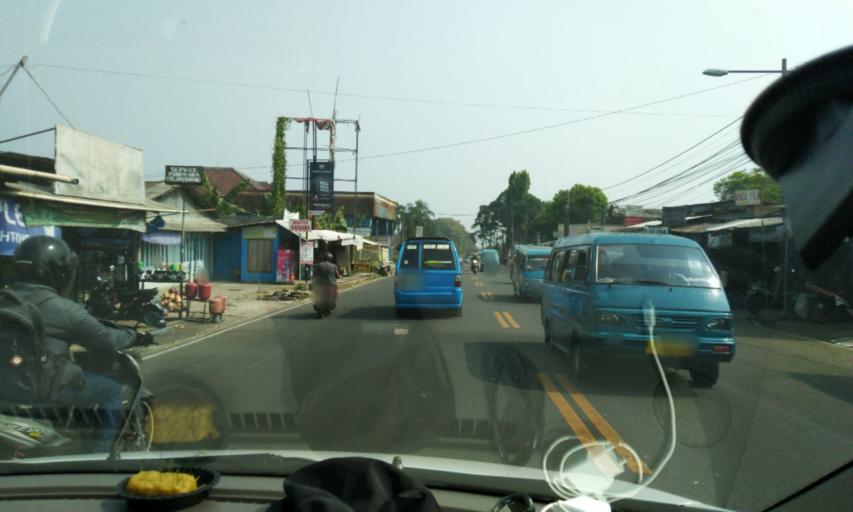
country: ID
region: West Java
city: Caringin
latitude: -6.6596
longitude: 106.8510
